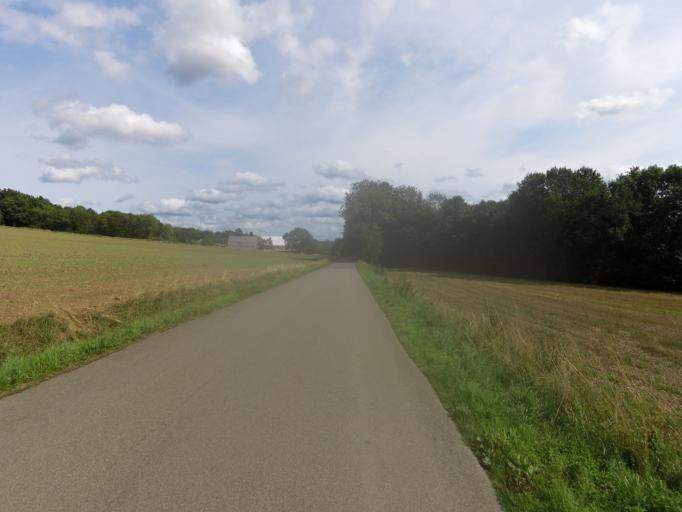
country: BE
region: Wallonia
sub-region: Province du Luxembourg
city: Durbuy
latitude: 50.3460
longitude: 5.4632
